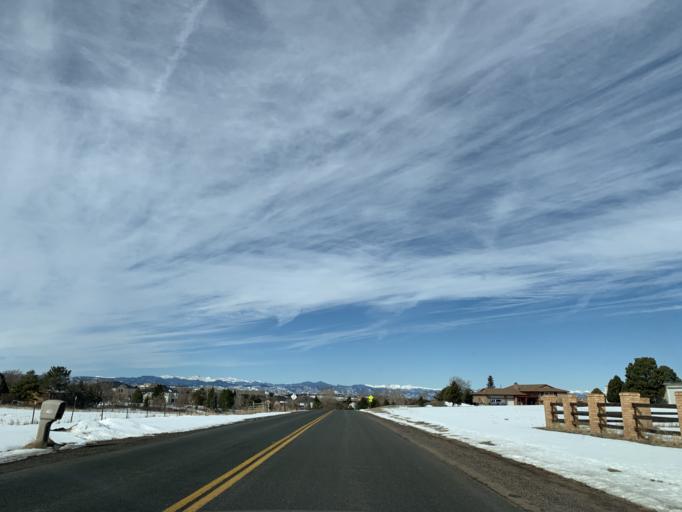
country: US
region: Colorado
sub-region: Douglas County
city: Carriage Club
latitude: 39.5189
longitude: -104.9114
